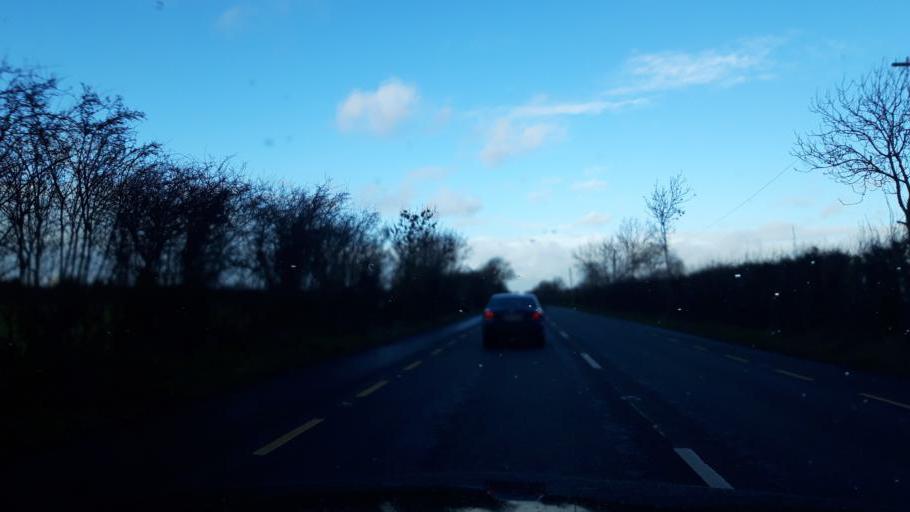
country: IE
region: Leinster
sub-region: An Mhi
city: Ratoath
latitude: 53.5851
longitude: -6.4594
